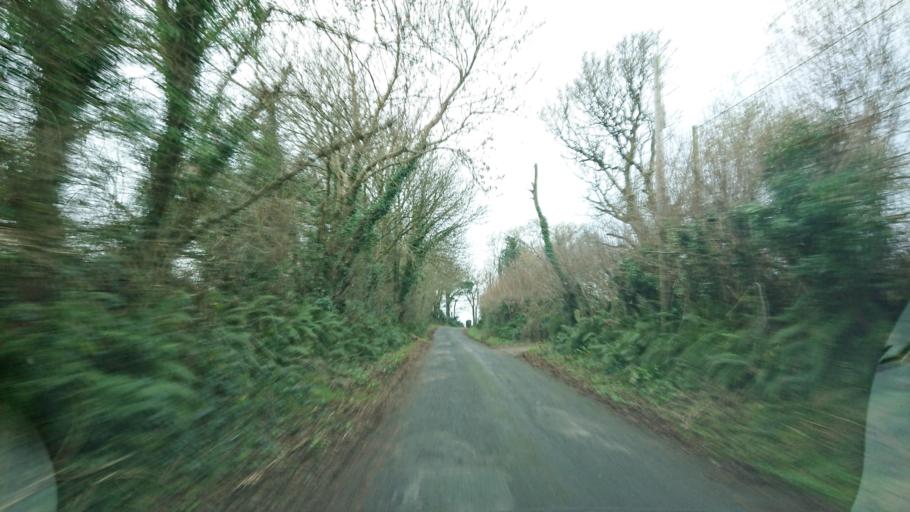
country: IE
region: Leinster
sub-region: Kilkenny
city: Mooncoin
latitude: 52.2281
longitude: -7.2571
